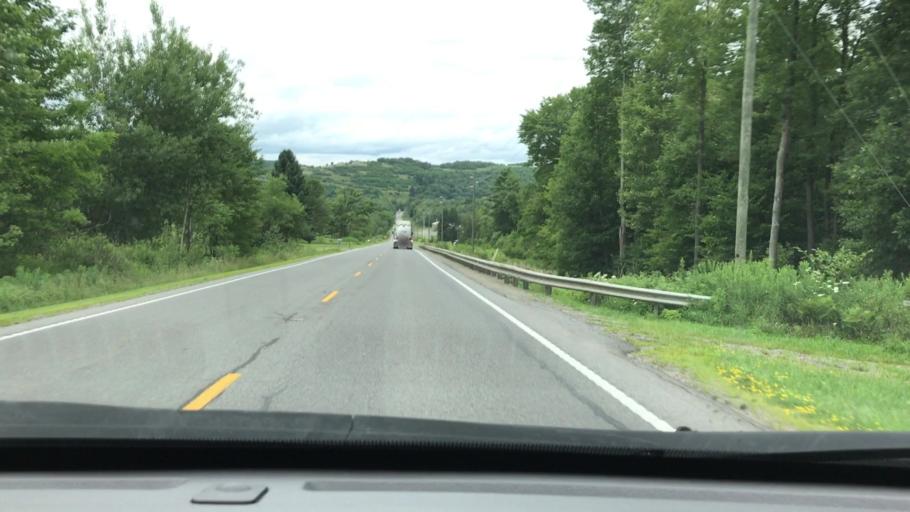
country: US
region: Pennsylvania
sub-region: Clearfield County
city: Treasure Lake
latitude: 41.2687
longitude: -78.6893
